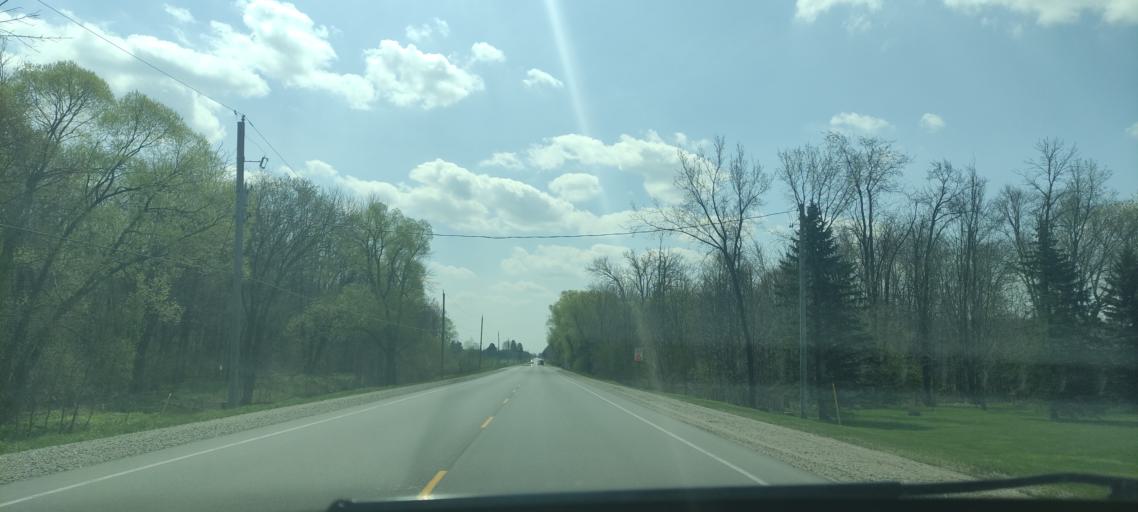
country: CA
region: Ontario
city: Stratford
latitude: 43.3433
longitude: -80.9999
